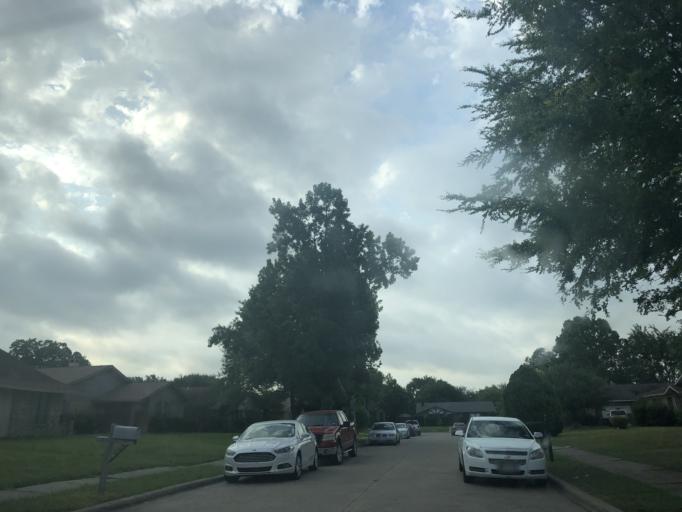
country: US
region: Texas
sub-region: Dallas County
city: Garland
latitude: 32.8449
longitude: -96.6240
